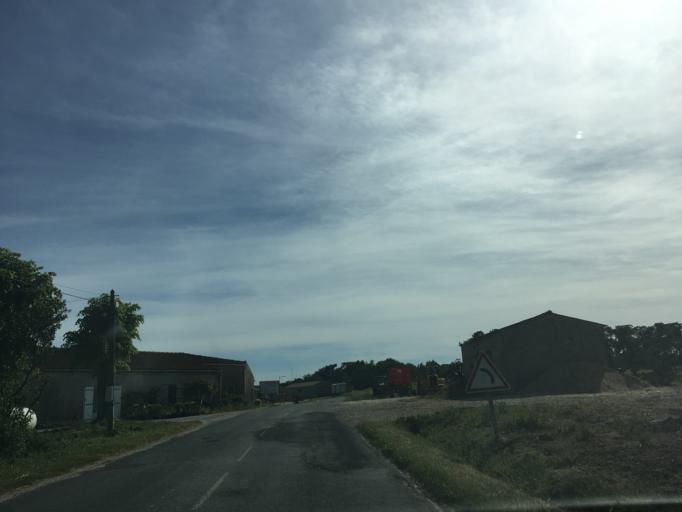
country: FR
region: Poitou-Charentes
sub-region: Departement de la Charente-Maritime
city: Mirambeau
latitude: 45.3360
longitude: -0.5922
